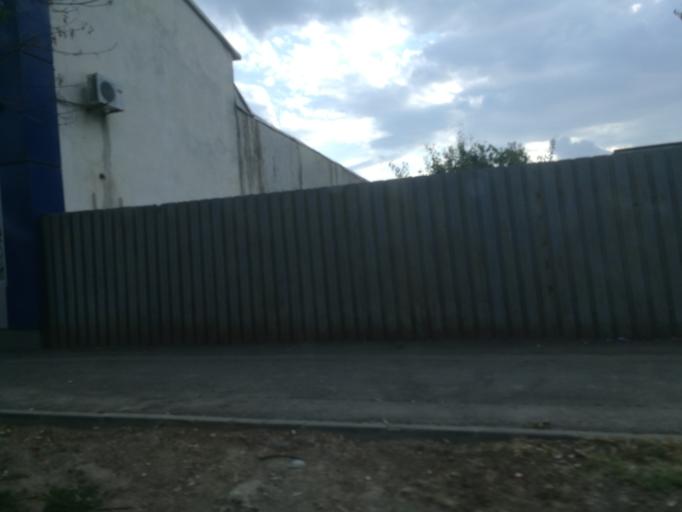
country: RO
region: Ilfov
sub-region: Comuna Mogosoaia
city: Mogosoaia
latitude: 44.4983
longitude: 26.0287
